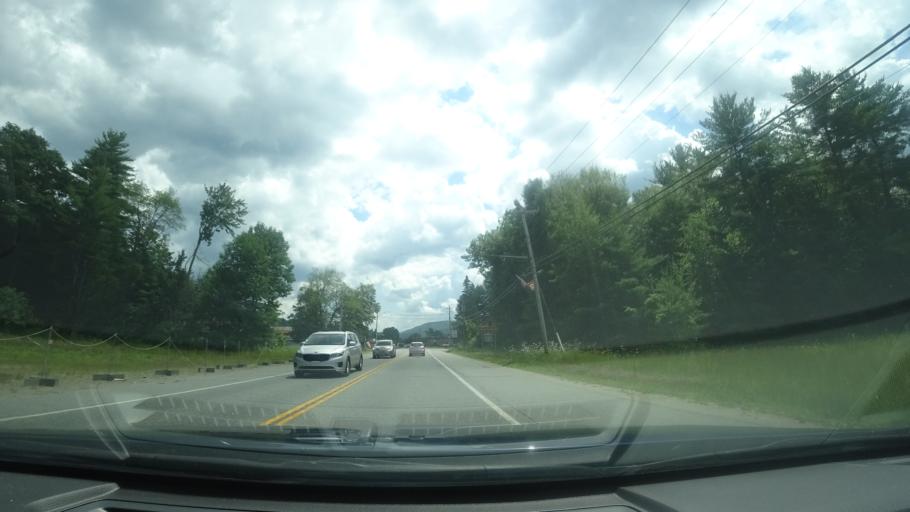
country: US
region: New York
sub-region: Warren County
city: Warrensburg
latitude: 43.5057
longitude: -73.7884
